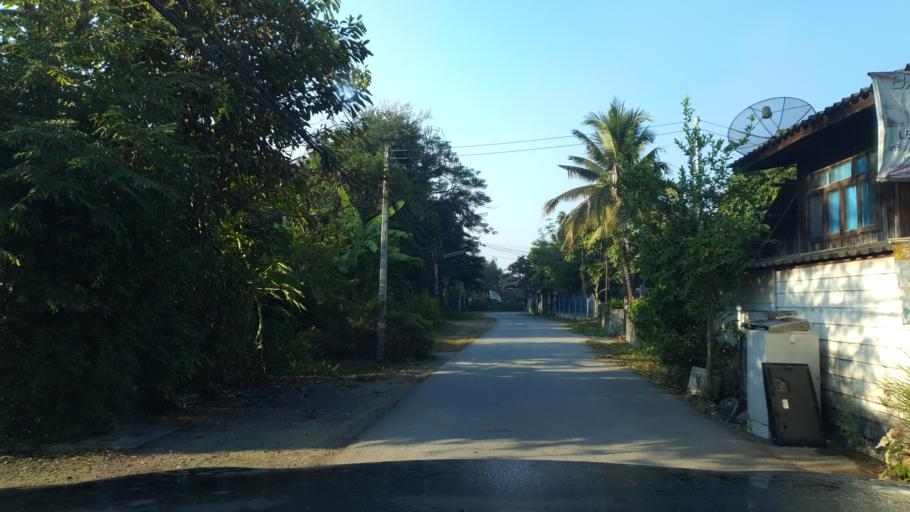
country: TH
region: Chiang Mai
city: San Kamphaeng
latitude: 18.7212
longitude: 99.1508
